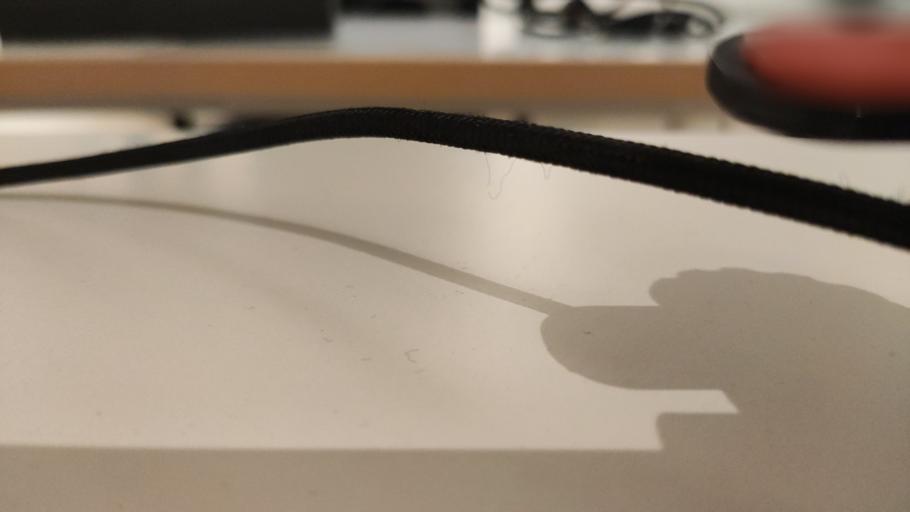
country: RU
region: Moskovskaya
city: Dorokhovo
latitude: 55.4889
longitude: 36.3557
